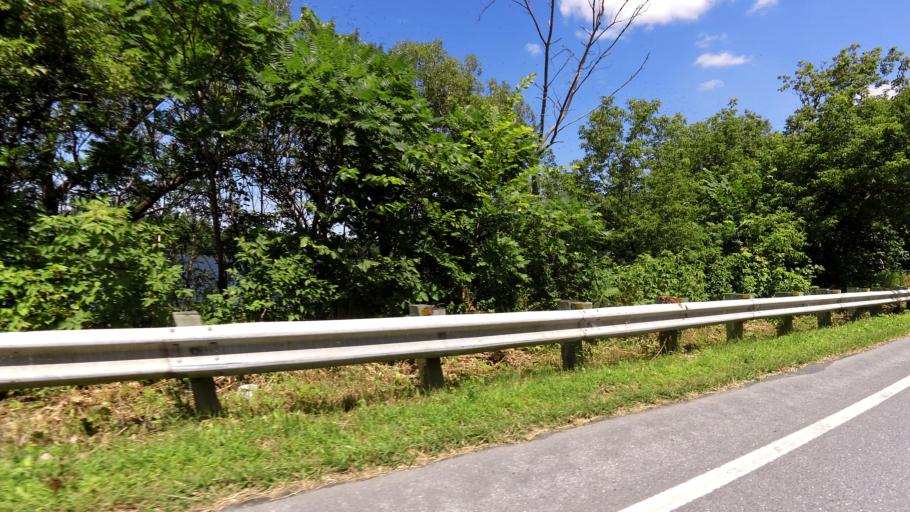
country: CA
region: Quebec
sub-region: Monteregie
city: Richelieu
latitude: 45.4041
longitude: -73.2510
